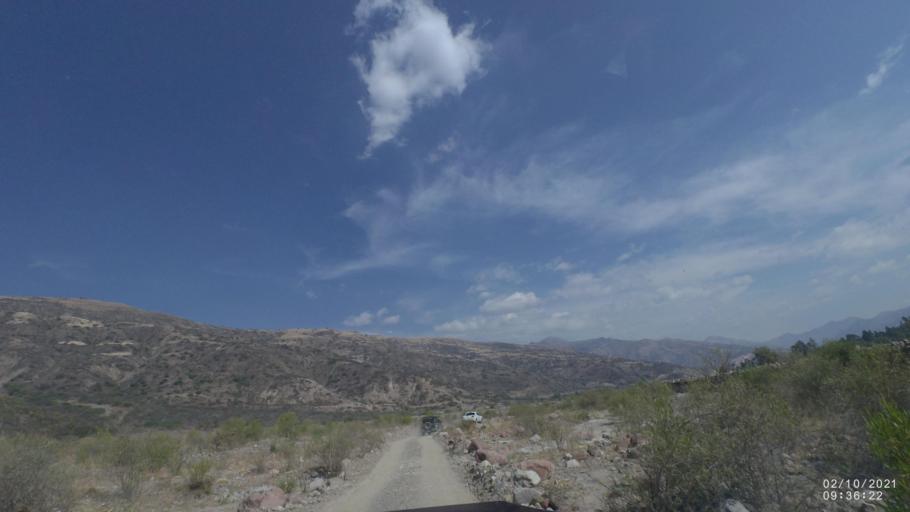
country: BO
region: Cochabamba
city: Irpa Irpa
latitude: -17.8328
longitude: -66.3210
